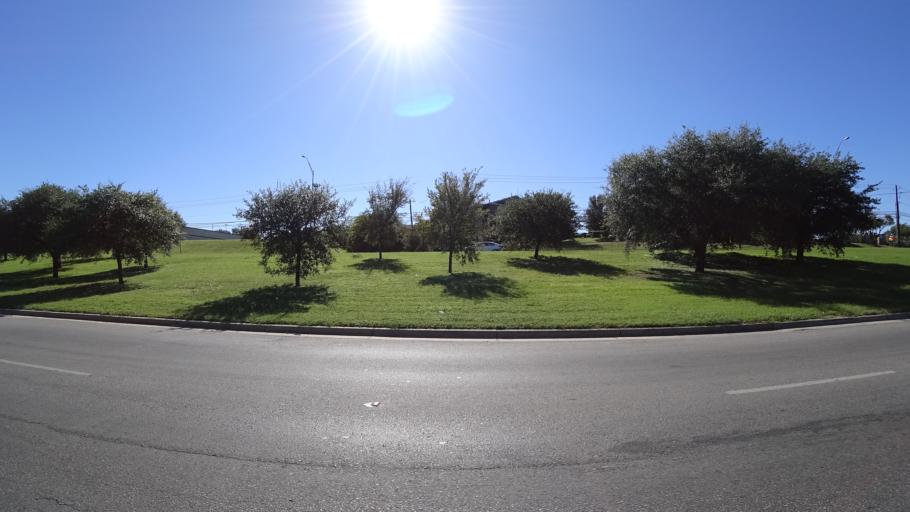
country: US
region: Texas
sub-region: Travis County
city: Austin
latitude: 30.2355
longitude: -97.7243
